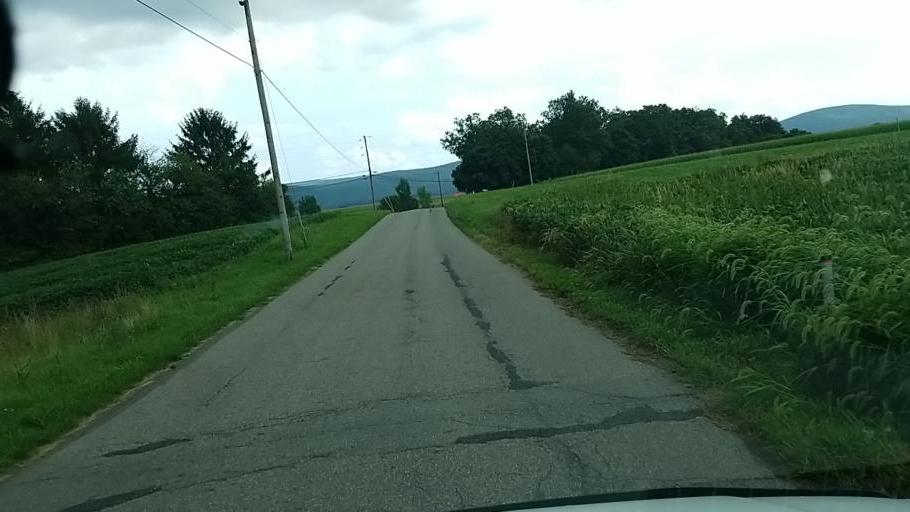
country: US
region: Pennsylvania
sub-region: Dauphin County
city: Elizabethville
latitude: 40.5833
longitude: -76.8162
